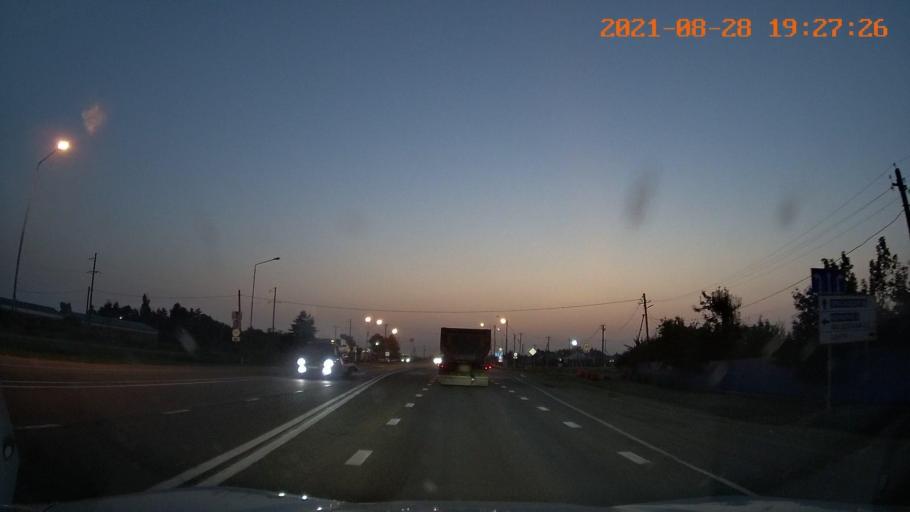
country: RU
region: Adygeya
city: Ponezhukay
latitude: 44.8787
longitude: 39.3831
